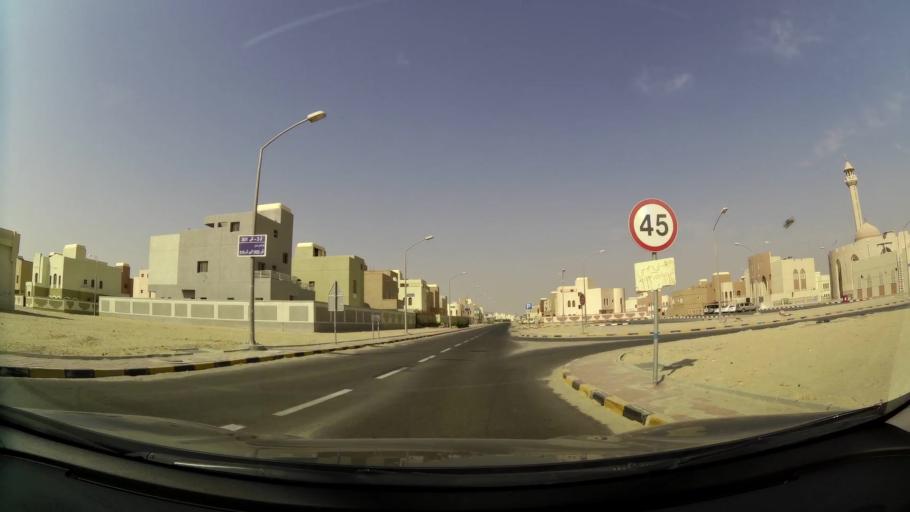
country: KW
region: Al Ahmadi
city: Al Wafrah
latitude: 28.8038
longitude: 48.0682
